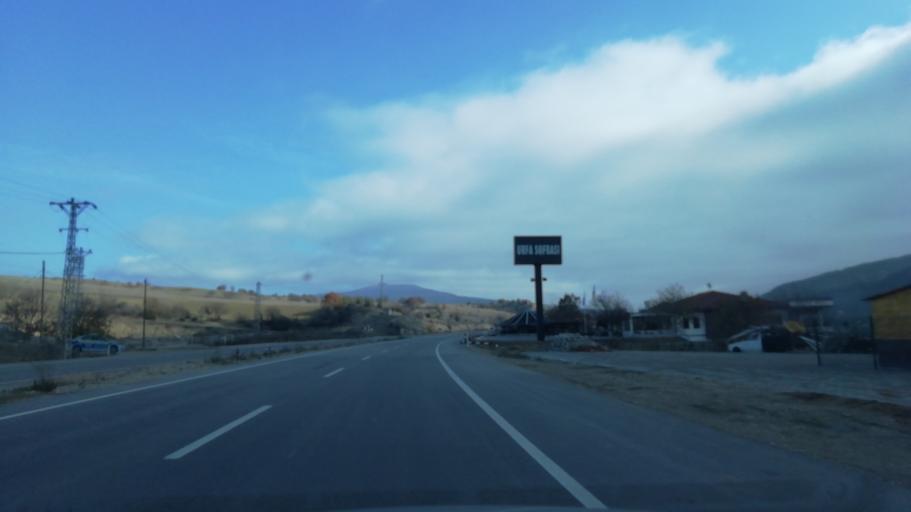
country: TR
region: Karabuk
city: Safranbolu
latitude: 41.2182
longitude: 32.7431
